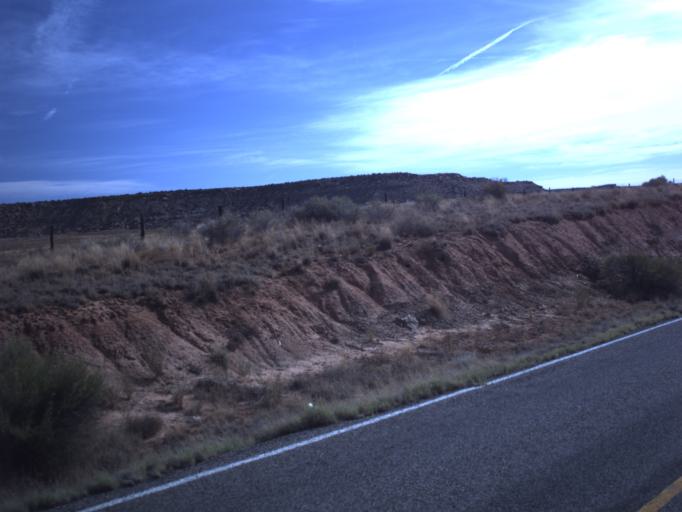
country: US
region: Utah
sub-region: San Juan County
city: Blanding
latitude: 37.4196
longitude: -109.4573
